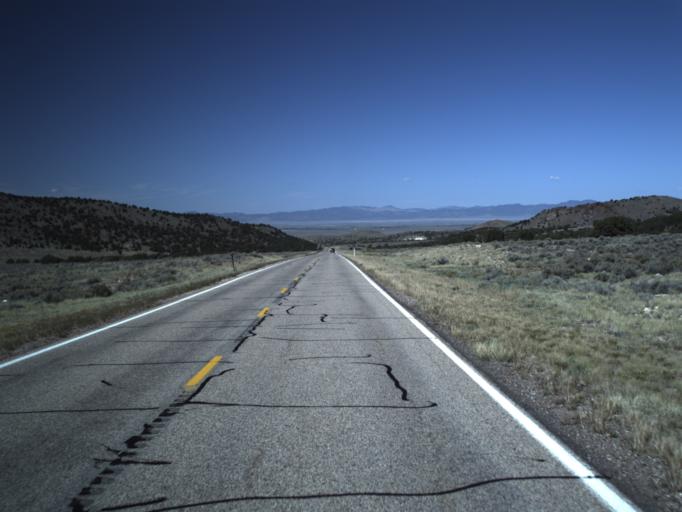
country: US
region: Utah
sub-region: Washington County
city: Enterprise
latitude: 37.6668
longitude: -113.4769
